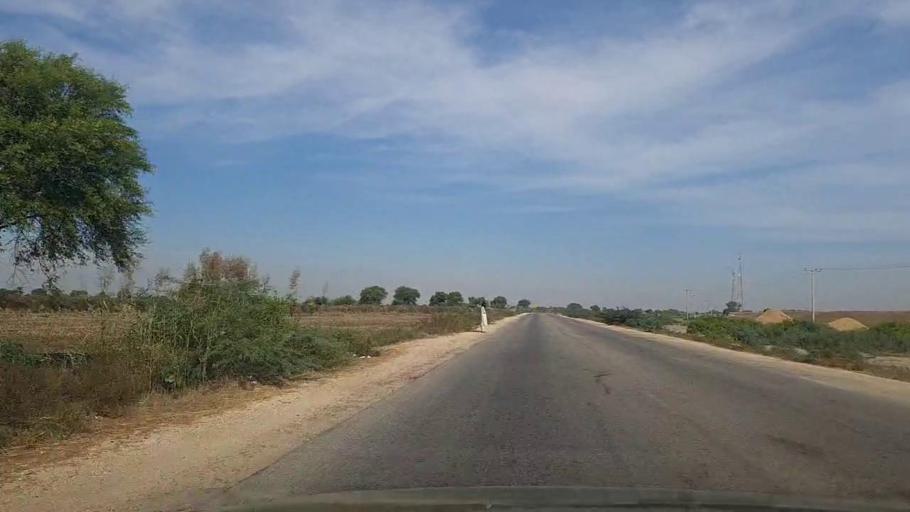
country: PK
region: Sindh
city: Daro Mehar
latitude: 24.9625
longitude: 68.1180
